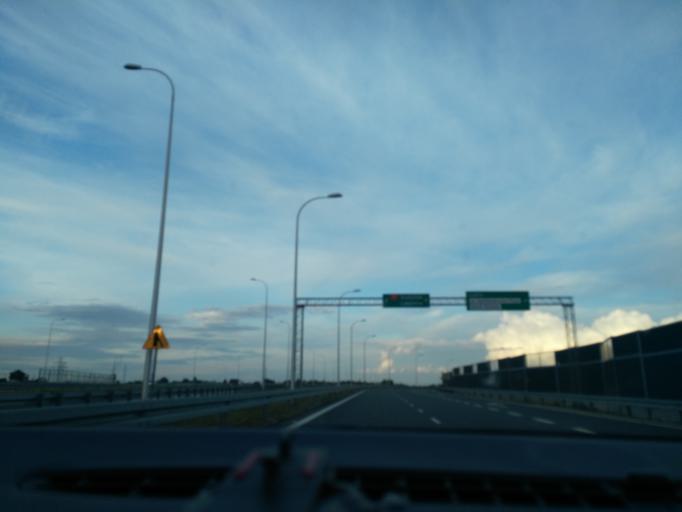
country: PL
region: Lublin Voivodeship
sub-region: Powiat lubelski
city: Lublin
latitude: 51.3027
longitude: 22.5804
